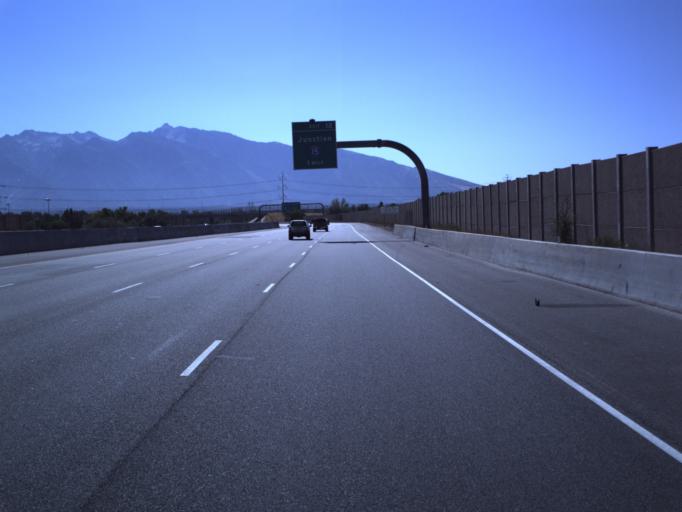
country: US
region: Utah
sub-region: Salt Lake County
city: Taylorsville
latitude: 40.6419
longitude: -111.9259
